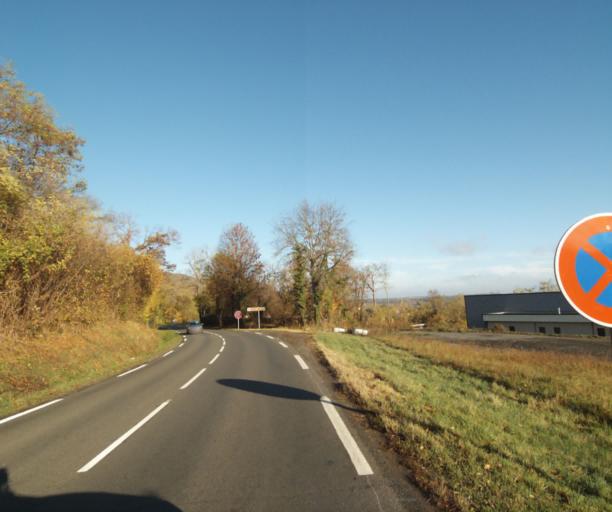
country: FR
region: Auvergne
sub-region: Departement du Puy-de-Dome
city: Durtol
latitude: 45.8027
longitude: 3.0514
